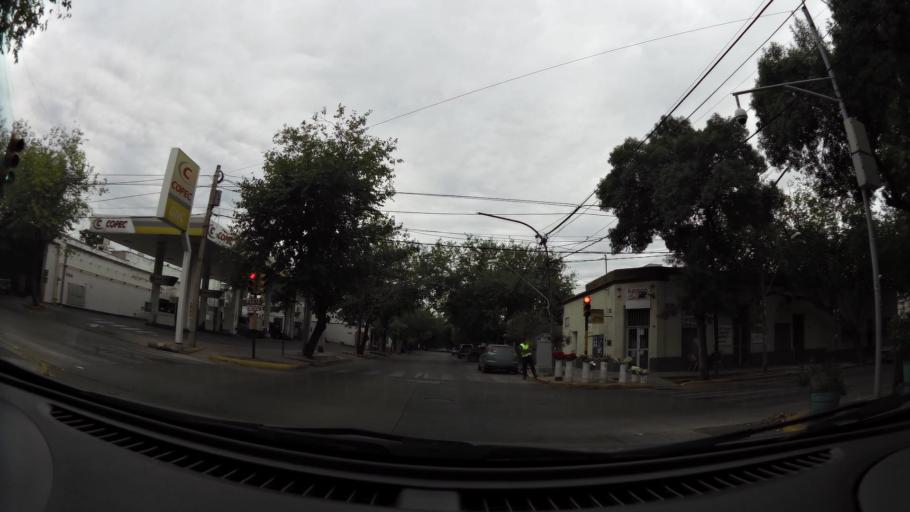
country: AR
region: Mendoza
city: Mendoza
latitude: -32.8861
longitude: -68.8511
